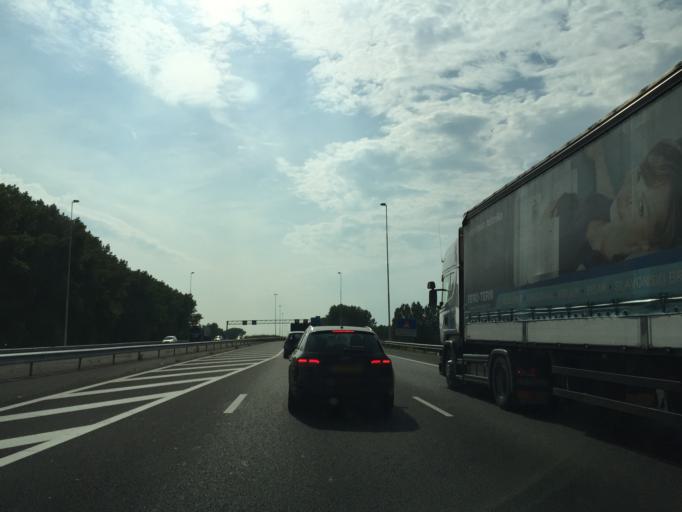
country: NL
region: Utrecht
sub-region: Gemeente Vianen
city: Vianen
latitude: 51.9557
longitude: 5.0598
